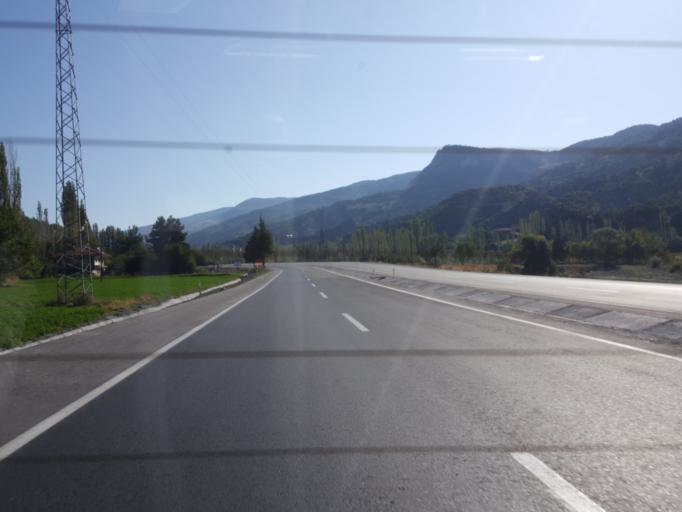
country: TR
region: Tokat
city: Turhal
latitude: 40.4748
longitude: 36.1422
